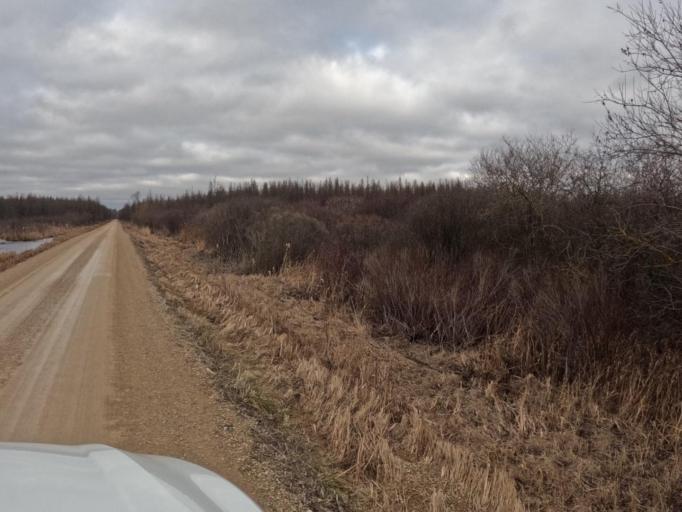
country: CA
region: Ontario
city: Shelburne
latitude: 43.8967
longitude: -80.4078
